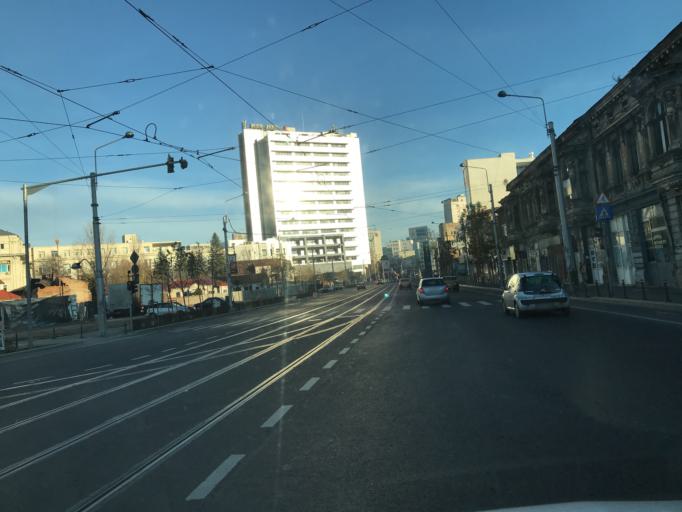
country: RO
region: Bucuresti
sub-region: Municipiul Bucuresti
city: Bucuresti
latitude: 44.4458
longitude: 26.0816
